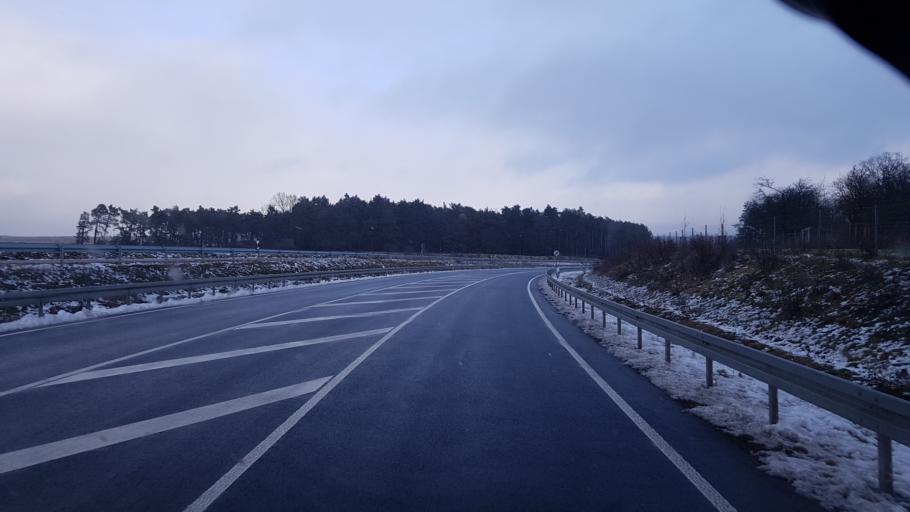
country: DE
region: Brandenburg
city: Heinersbruck
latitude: 51.8555
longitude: 14.5972
